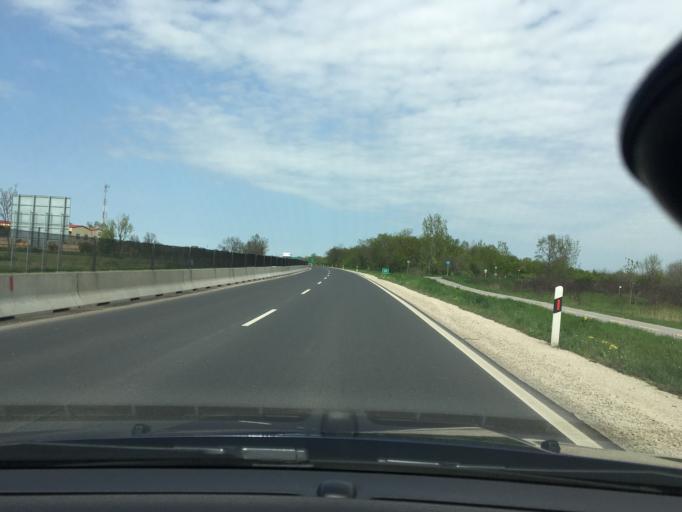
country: HU
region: Csongrad
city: Algyo
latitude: 46.3178
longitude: 20.1909
